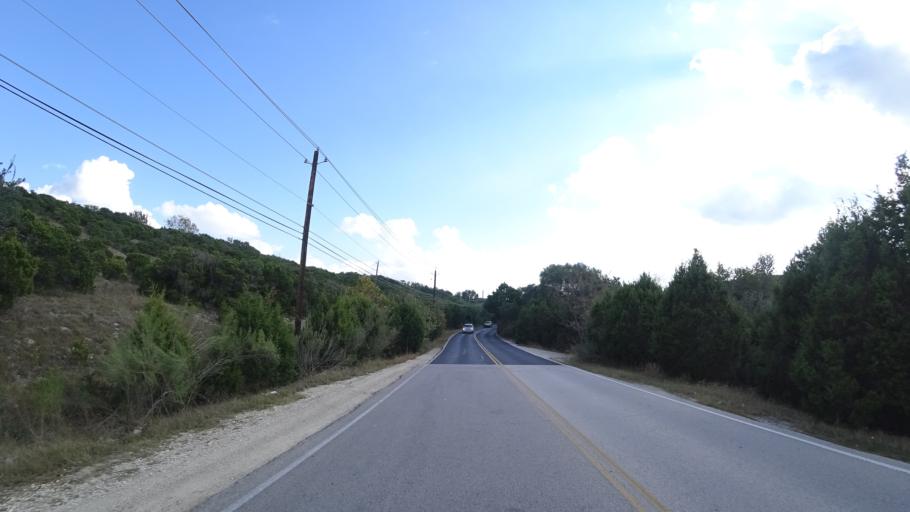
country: US
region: Texas
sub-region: Travis County
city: Barton Creek
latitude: 30.2611
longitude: -97.8888
